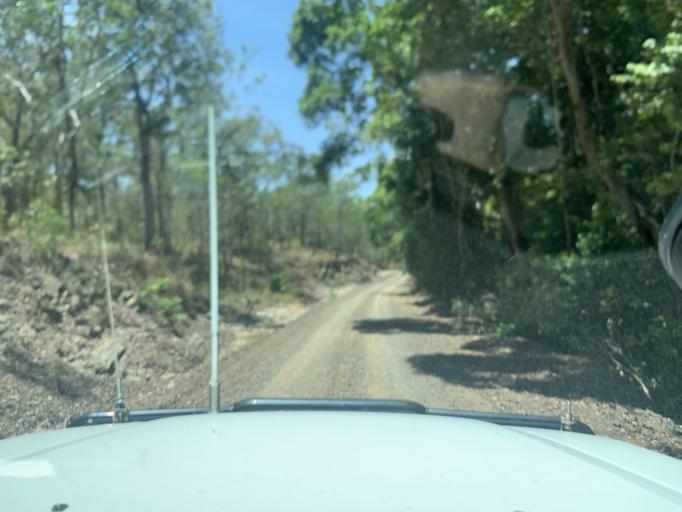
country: AU
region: Queensland
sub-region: Cairns
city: Redlynch
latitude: -16.9310
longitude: 145.6017
